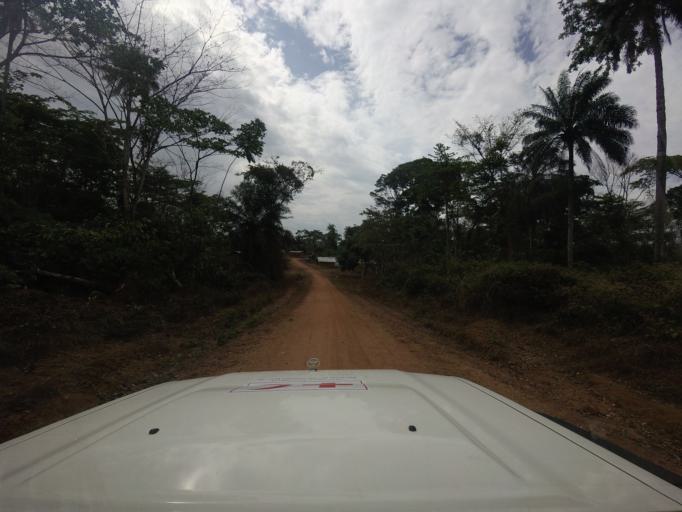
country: SL
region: Eastern Province
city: Buedu
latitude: 8.2674
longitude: -10.2370
